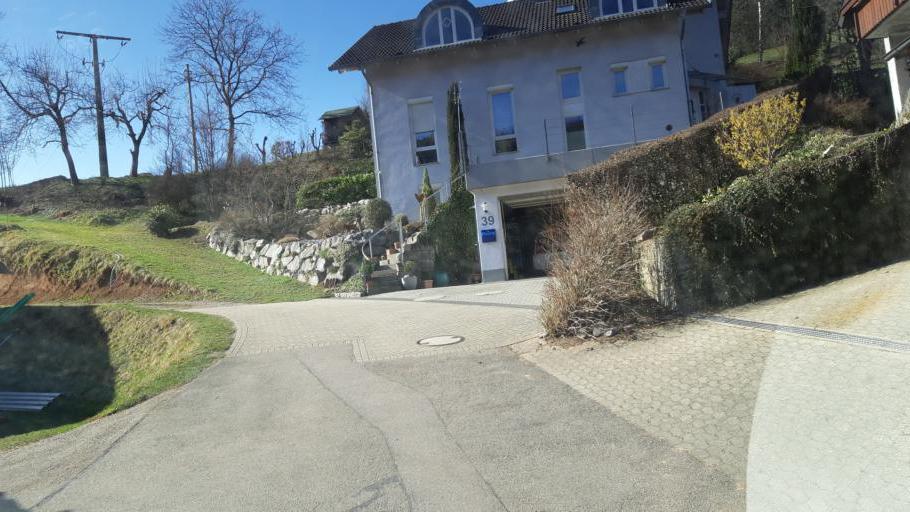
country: DE
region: Baden-Wuerttemberg
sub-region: Freiburg Region
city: Gutach im Breisgau
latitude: 48.1471
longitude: 7.9773
